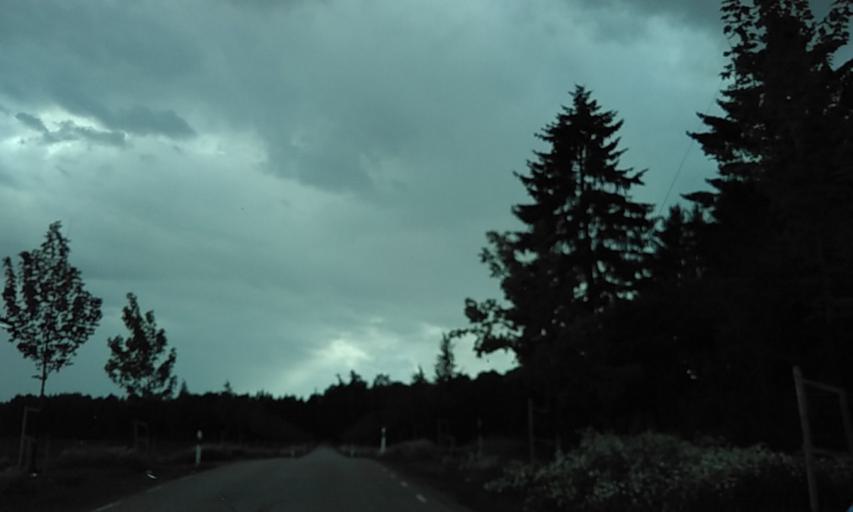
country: SE
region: Vaestra Goetaland
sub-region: Grastorps Kommun
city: Graestorp
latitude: 58.4685
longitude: 12.8138
